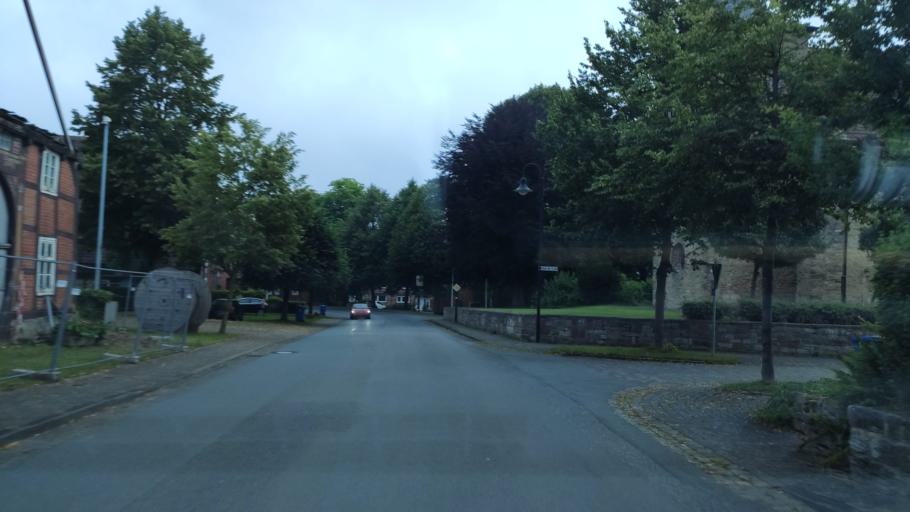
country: DE
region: North Rhine-Westphalia
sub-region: Regierungsbezirk Detmold
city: Schieder-Schwalenberg
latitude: 51.8398
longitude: 9.1753
